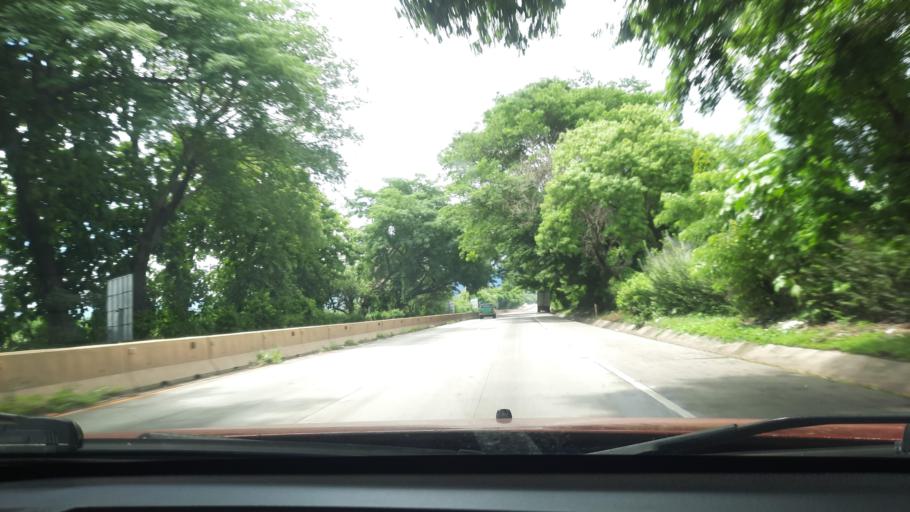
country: SV
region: Sonsonate
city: Sonsonate
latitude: 13.7164
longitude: -89.7089
